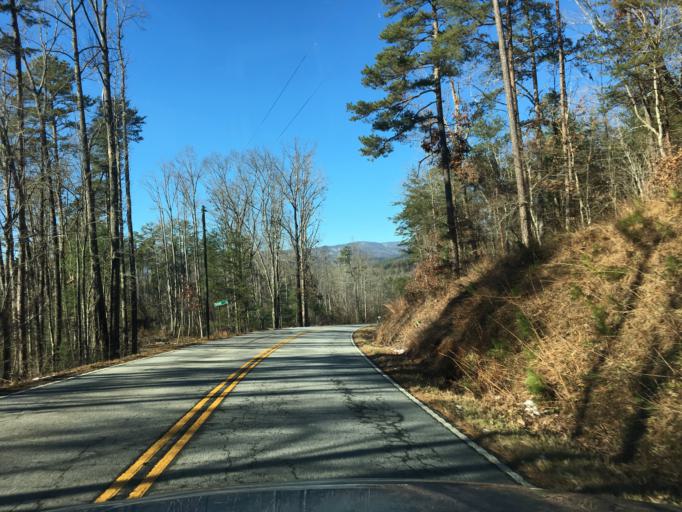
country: US
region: South Carolina
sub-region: Oconee County
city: Walhalla
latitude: 34.9254
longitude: -82.9853
